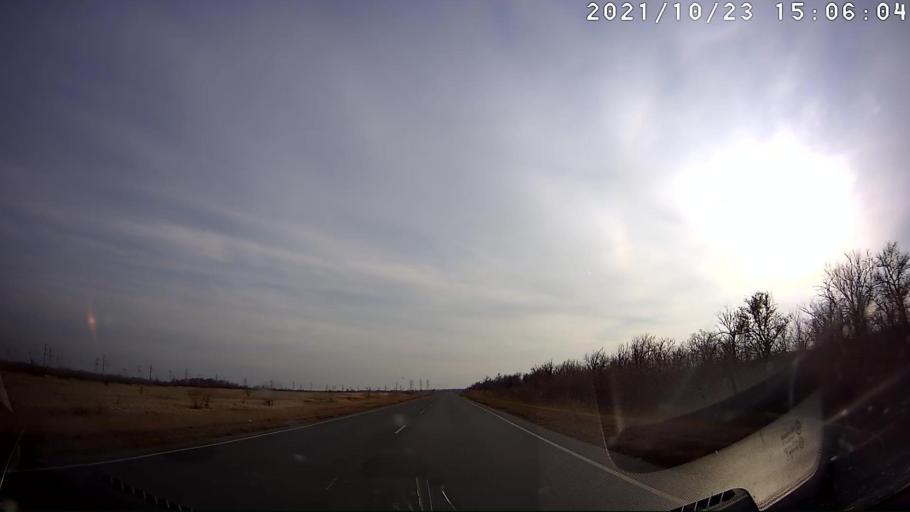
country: RU
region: Volgograd
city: Volgograd
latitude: 48.3754
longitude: 44.3587
